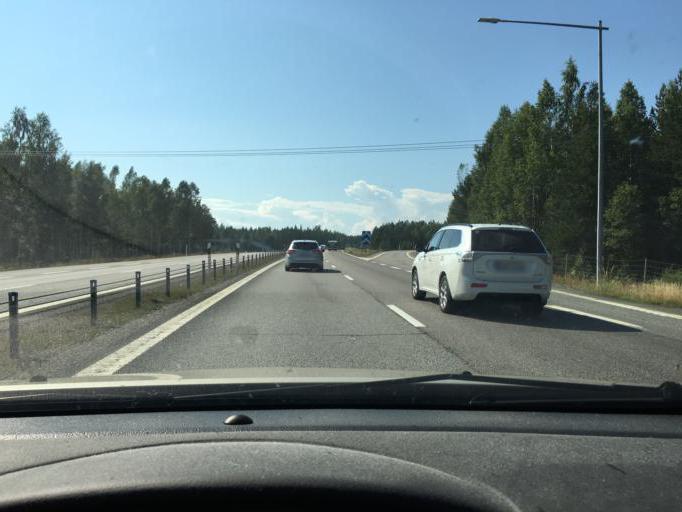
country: SE
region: Norrbotten
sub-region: Lulea Kommun
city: Gammelstad
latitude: 65.5840
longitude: 22.0036
